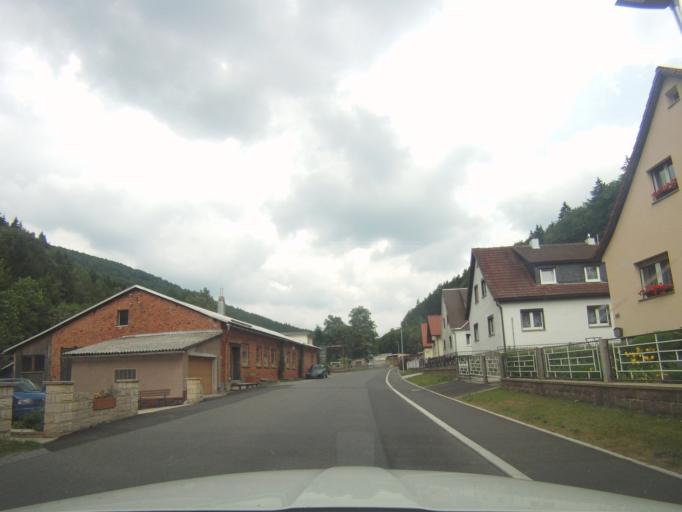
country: DE
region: Thuringia
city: Frauenwald
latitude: 50.5319
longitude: 10.8788
